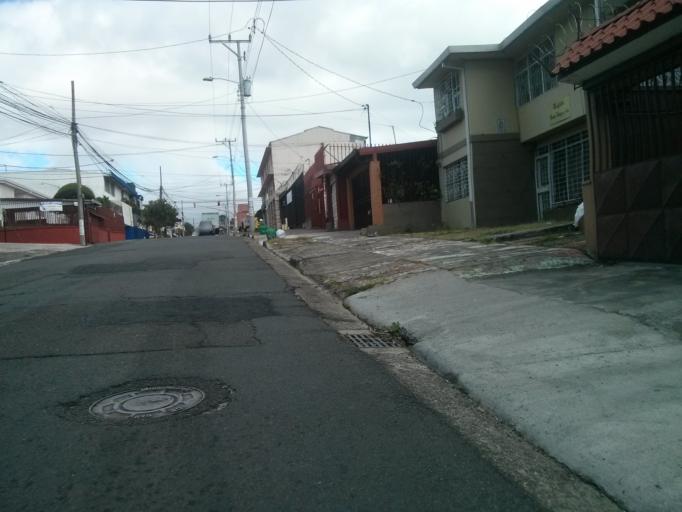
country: CR
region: San Jose
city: San Pedro
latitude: 9.9281
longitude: -84.0651
